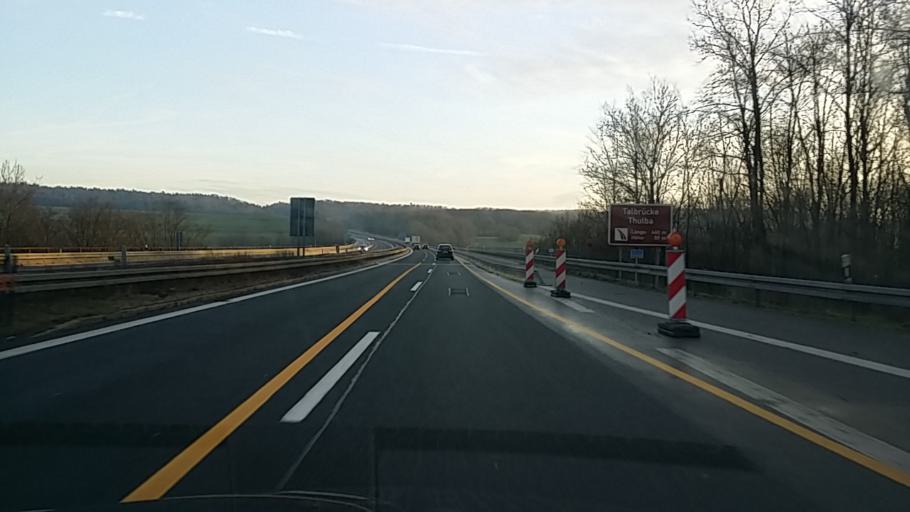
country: DE
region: Bavaria
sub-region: Regierungsbezirk Unterfranken
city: Oberthulba
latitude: 50.1941
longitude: 9.9410
